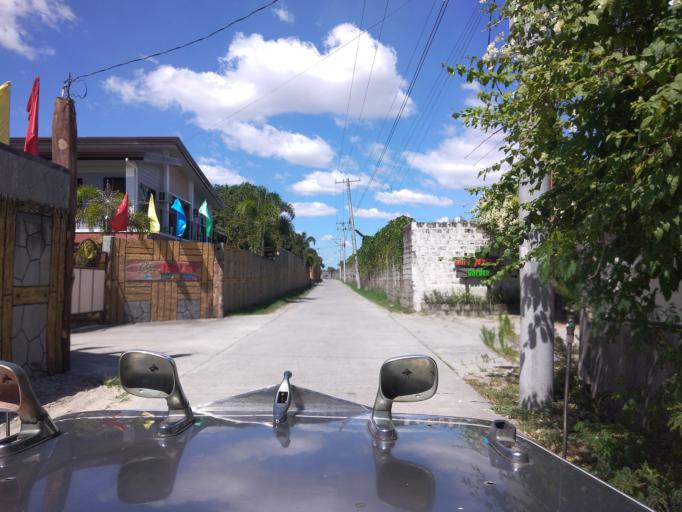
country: PH
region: Central Luzon
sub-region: Province of Pampanga
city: Magliman
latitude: 15.0535
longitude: 120.6405
